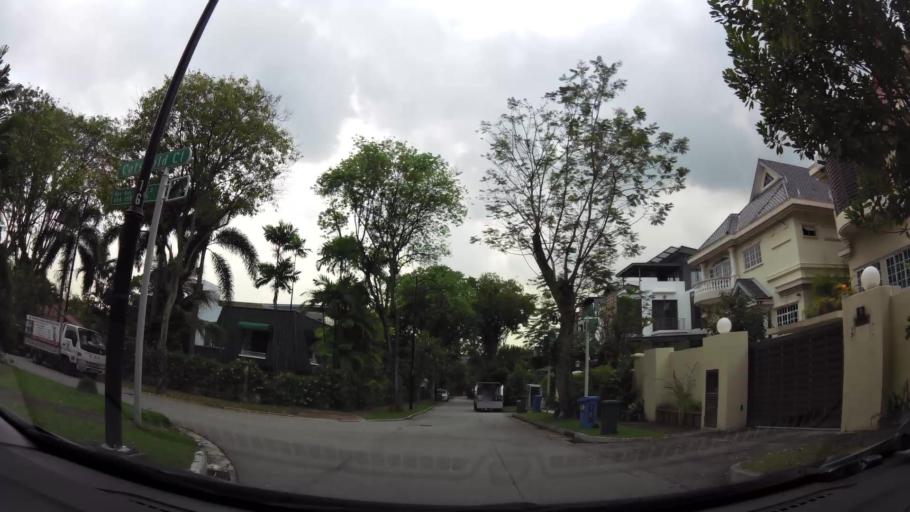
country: SG
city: Singapore
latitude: 1.3466
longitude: 103.8622
